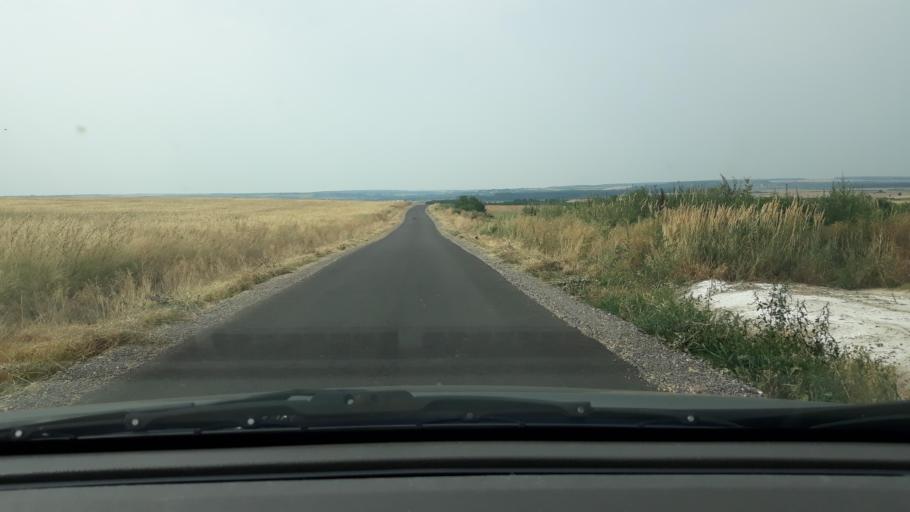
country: RO
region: Bihor
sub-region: Comuna Chislaz
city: Misca
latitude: 47.2734
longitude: 22.2830
